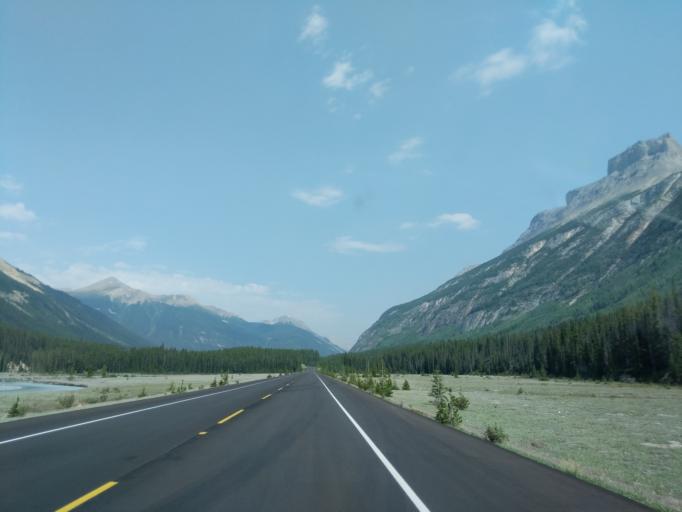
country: CA
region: British Columbia
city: Golden
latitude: 52.0841
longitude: -116.9349
